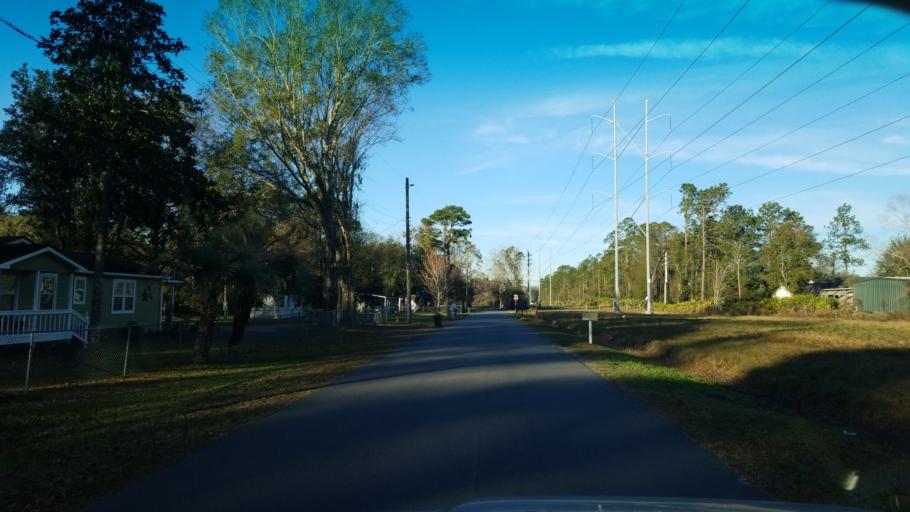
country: US
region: Florida
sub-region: Duval County
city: Baldwin
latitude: 30.3235
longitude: -81.8470
